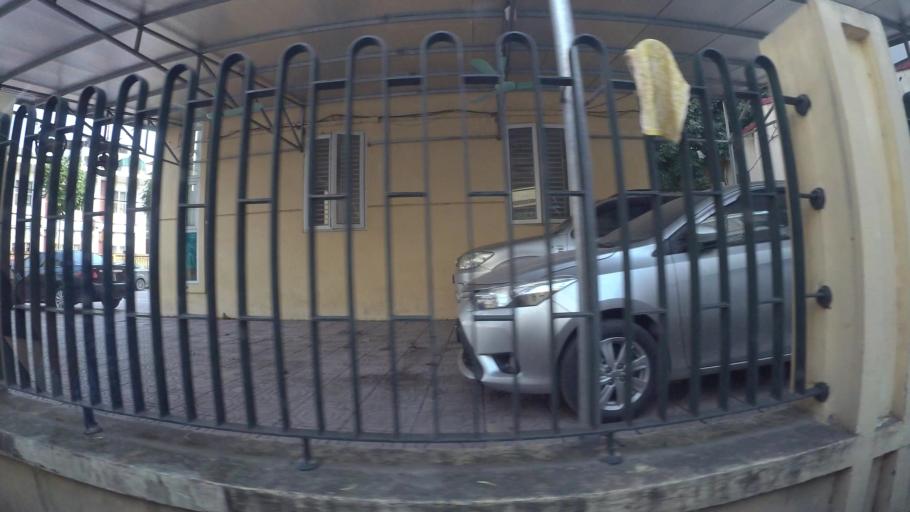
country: VN
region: Ha Noi
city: Thanh Xuan
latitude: 20.9799
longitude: 105.8280
